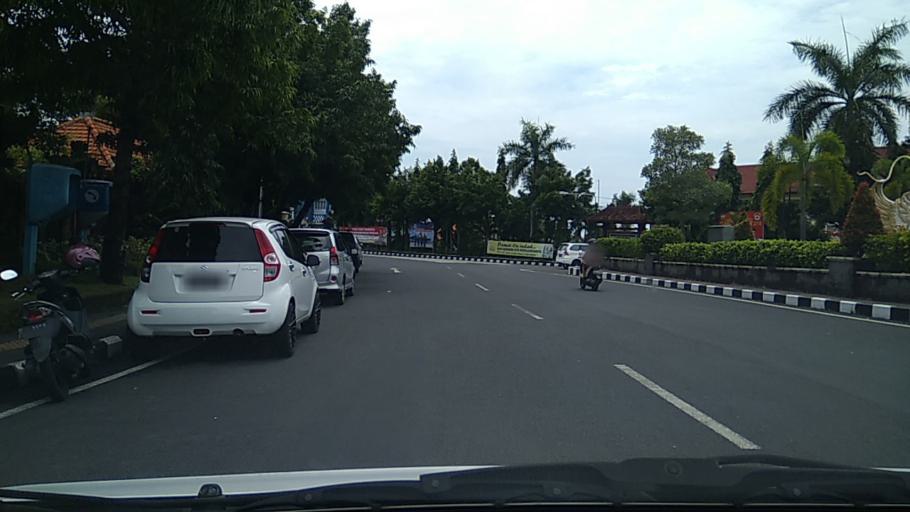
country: ID
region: Bali
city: Banjar Kelodan
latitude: -8.5409
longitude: 115.3230
